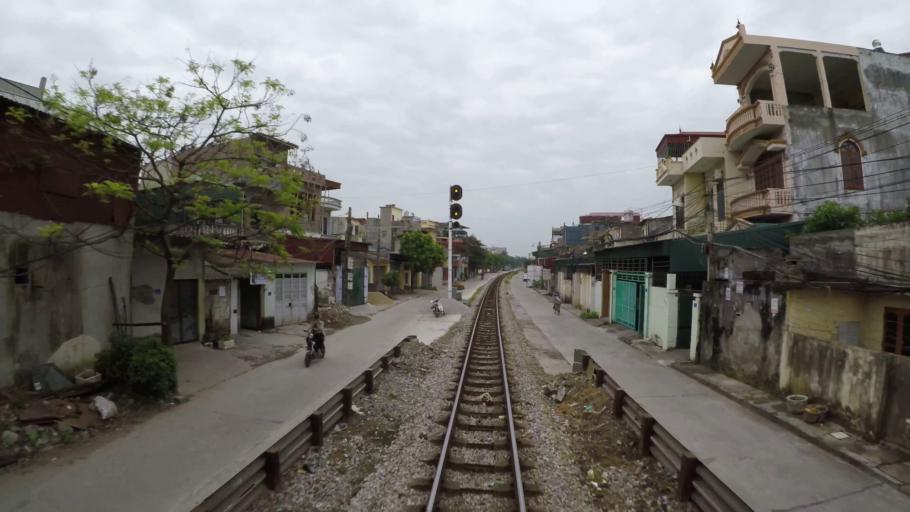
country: VN
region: Hai Duong
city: Lai Cach
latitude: 20.9432
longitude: 106.2891
